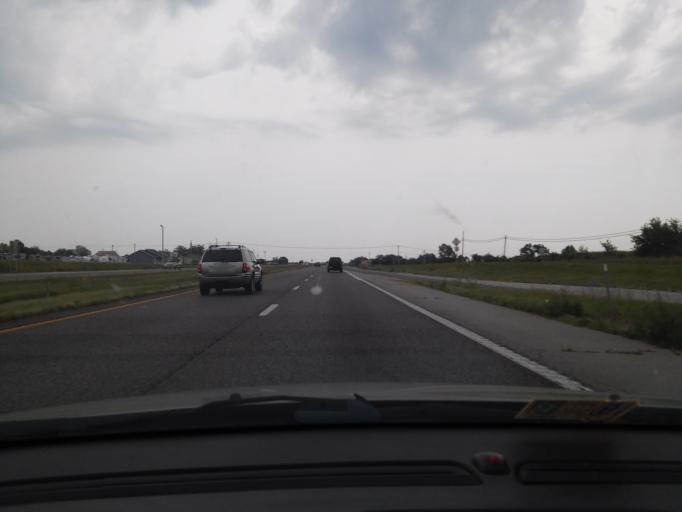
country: US
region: Missouri
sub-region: Boone County
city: Columbia
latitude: 38.9586
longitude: -92.2024
